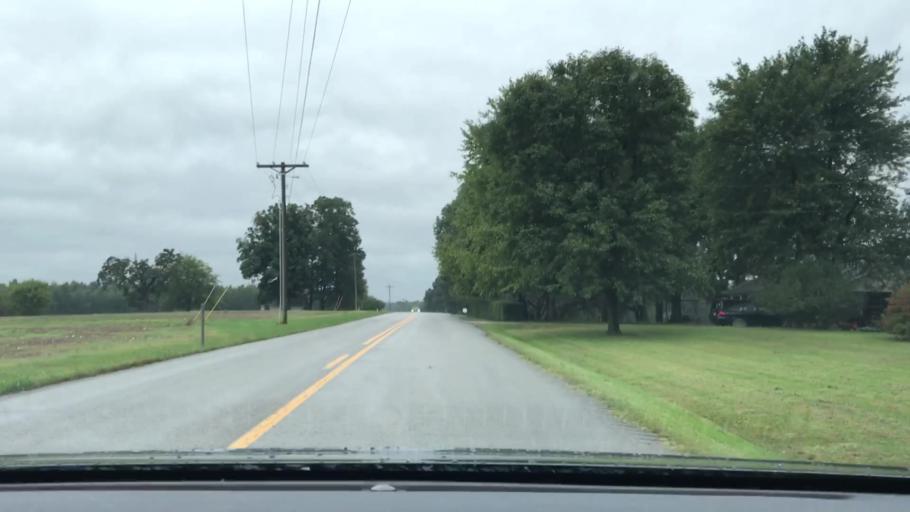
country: US
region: Kentucky
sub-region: McLean County
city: Calhoun
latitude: 37.4616
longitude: -87.2335
